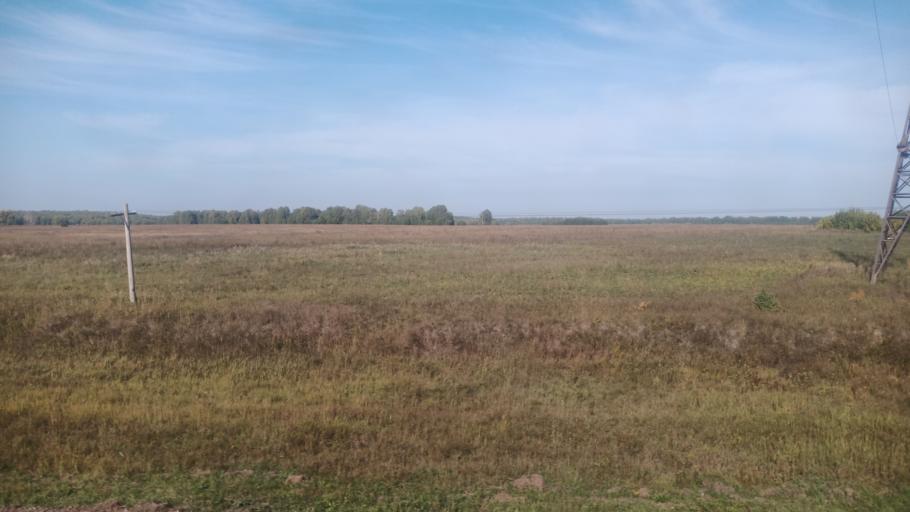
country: RU
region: Altai Krai
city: Troitskoye
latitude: 53.0992
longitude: 84.6748
